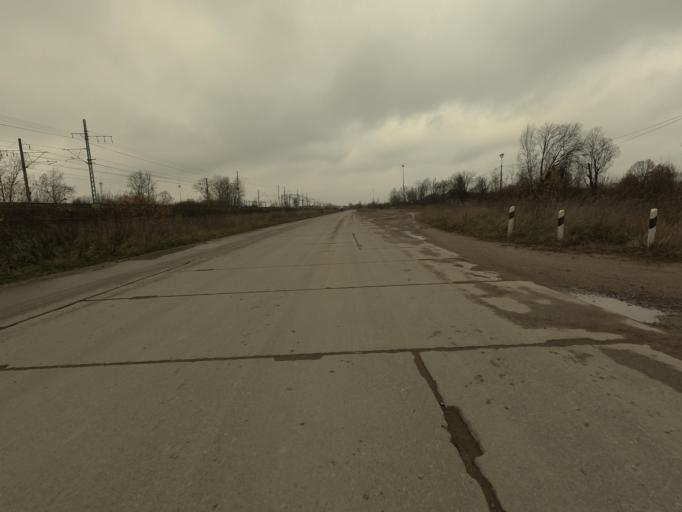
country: RU
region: Leningrad
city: Lyuban'
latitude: 59.4730
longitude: 31.2550
